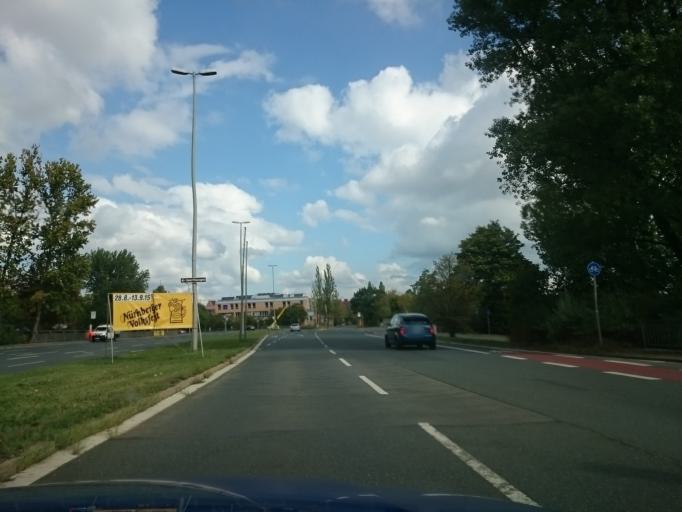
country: DE
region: Bavaria
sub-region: Regierungsbezirk Mittelfranken
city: Nuernberg
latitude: 49.4502
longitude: 11.0974
